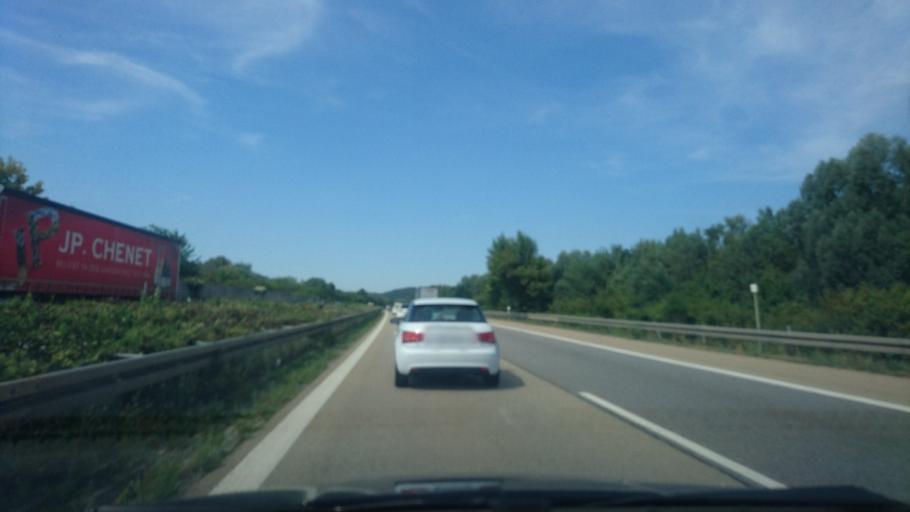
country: DE
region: Bavaria
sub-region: Upper Palatinate
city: Lappersdorf
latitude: 49.0590
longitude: 12.0928
